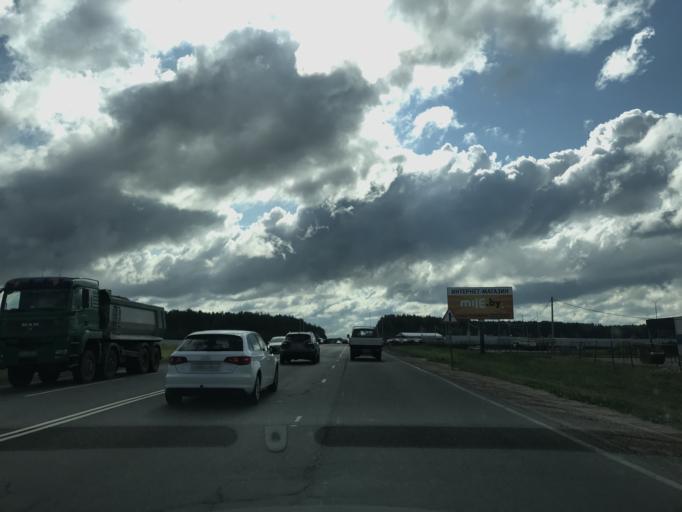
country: BY
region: Minsk
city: Borovlyany
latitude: 53.9682
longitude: 27.6253
